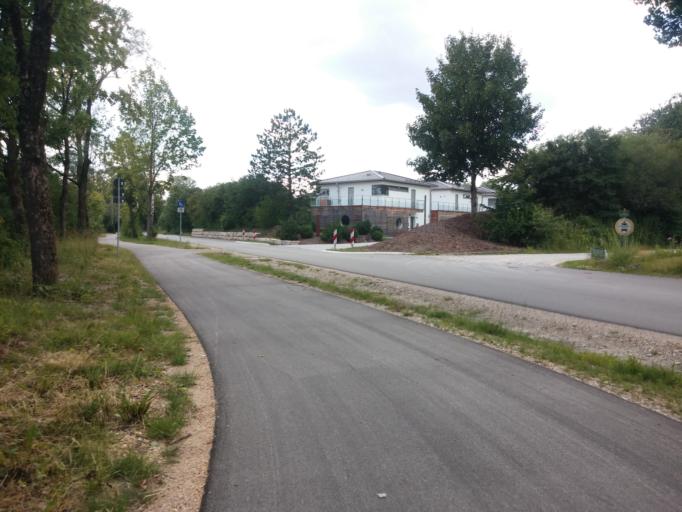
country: DE
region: Bavaria
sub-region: Upper Bavaria
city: Aschheim
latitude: 48.1799
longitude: 11.7056
